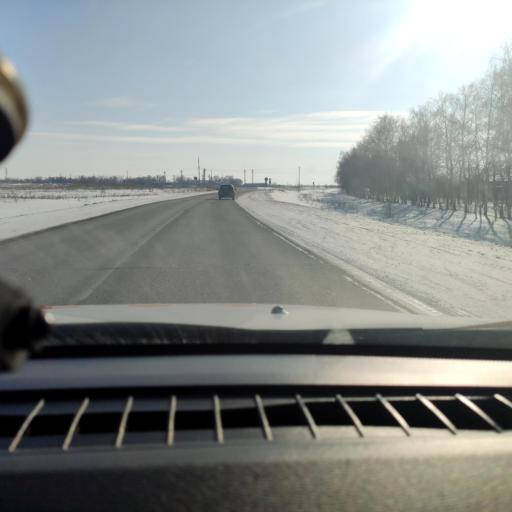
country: RU
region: Samara
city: Dubovyy Umet
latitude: 53.0875
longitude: 50.3492
